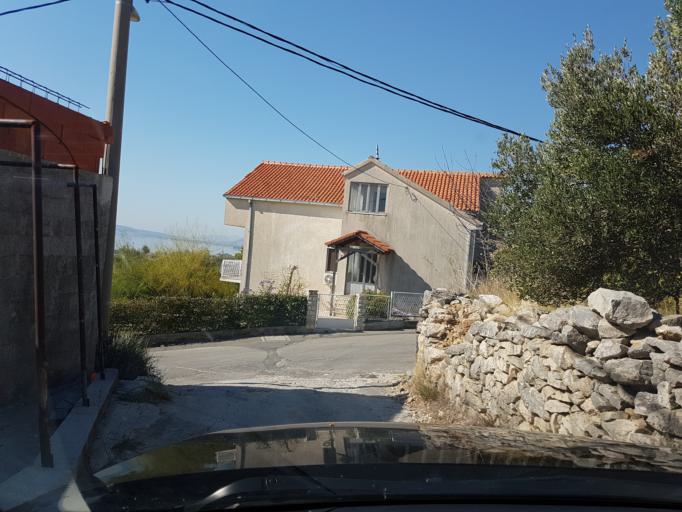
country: HR
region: Splitsko-Dalmatinska
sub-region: Grad Split
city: Split
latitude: 43.5597
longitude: 16.3862
